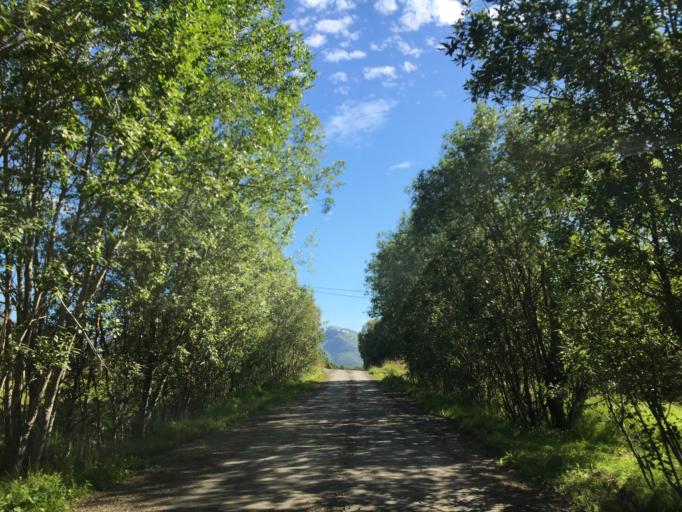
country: NO
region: Nordland
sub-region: Vagan
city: Kabelvag
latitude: 68.3520
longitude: 14.4516
